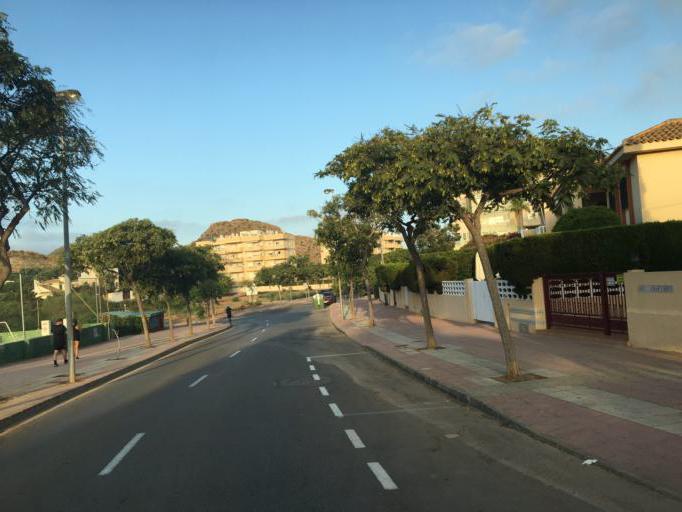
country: ES
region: Murcia
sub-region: Murcia
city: La Manga del Mar Menor
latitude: 37.6250
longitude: -0.7085
